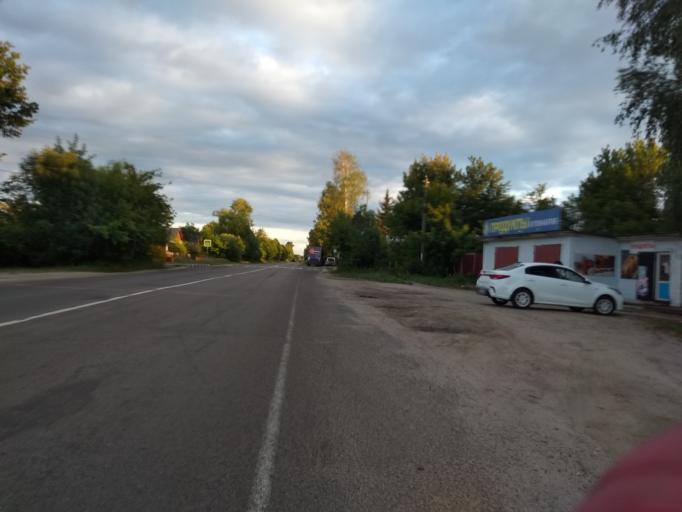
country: RU
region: Moskovskaya
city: Misheronskiy
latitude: 55.5992
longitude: 39.7050
